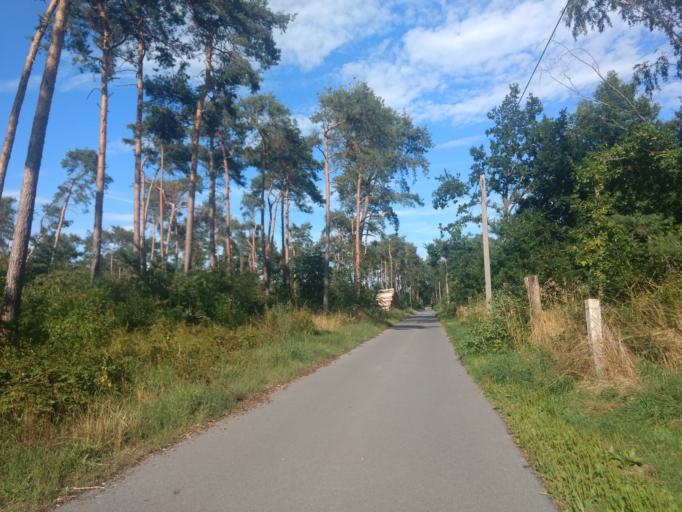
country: DE
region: North Rhine-Westphalia
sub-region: Regierungsbezirk Detmold
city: Delbruck
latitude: 51.7540
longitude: 8.6044
